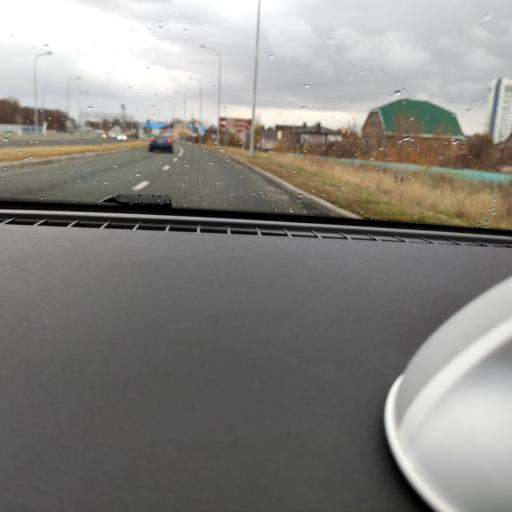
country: RU
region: Samara
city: Samara
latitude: 53.2721
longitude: 50.2327
